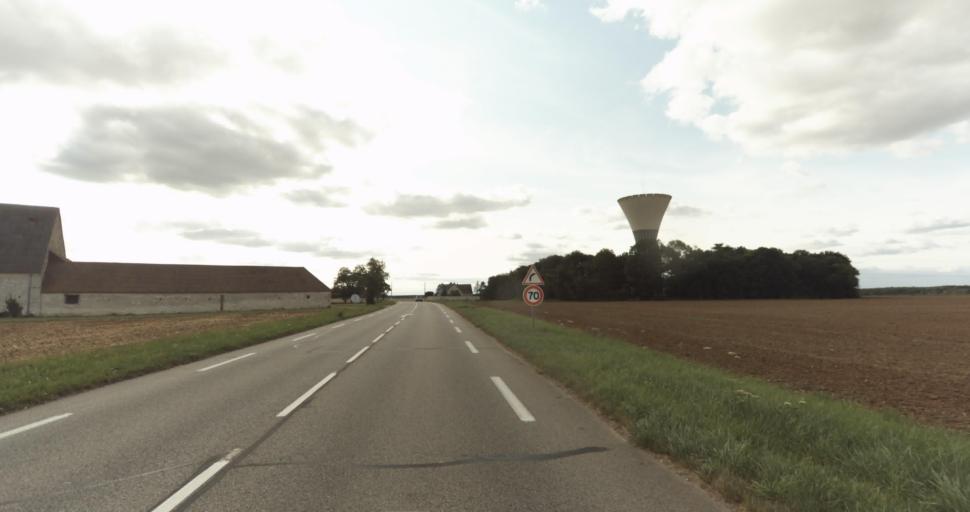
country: FR
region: Haute-Normandie
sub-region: Departement de l'Eure
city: Garennes-sur-Eure
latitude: 48.8914
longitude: 1.4320
